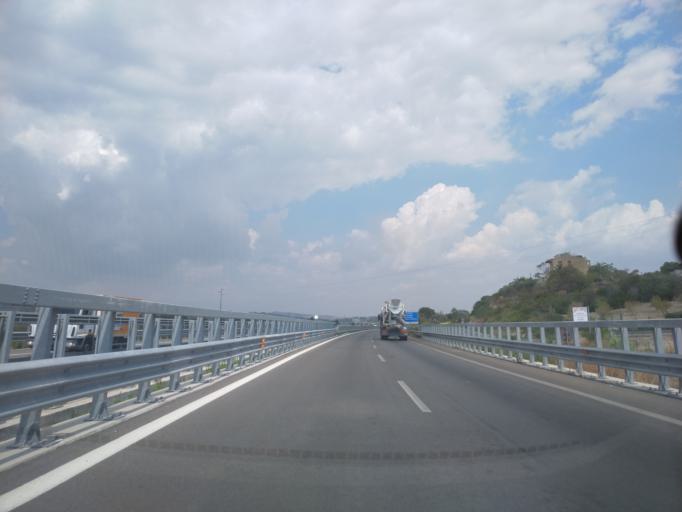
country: IT
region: Sicily
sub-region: Agrigento
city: Grotte
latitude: 37.3708
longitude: 13.7097
